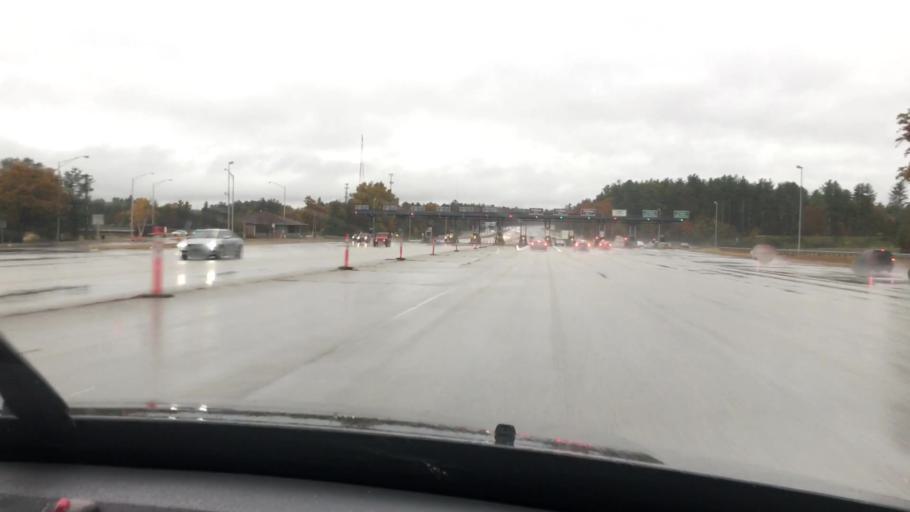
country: US
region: New Hampshire
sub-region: Hillsborough County
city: East Merrimack
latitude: 42.9167
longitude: -71.4656
